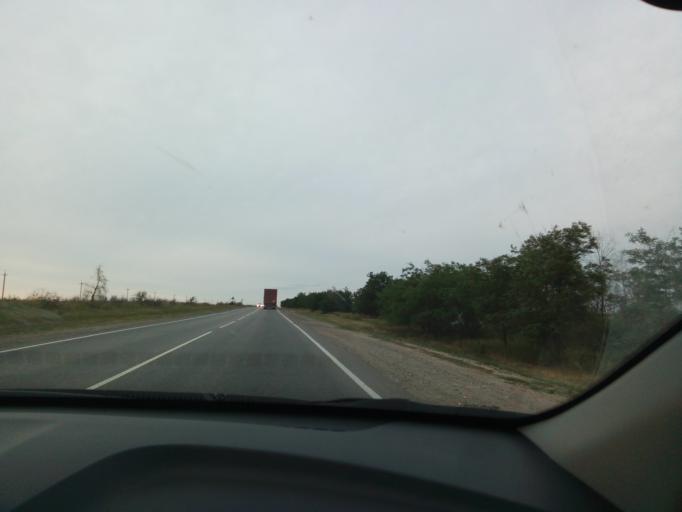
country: RU
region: Volgograd
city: Dubovka
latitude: 49.1407
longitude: 44.8274
